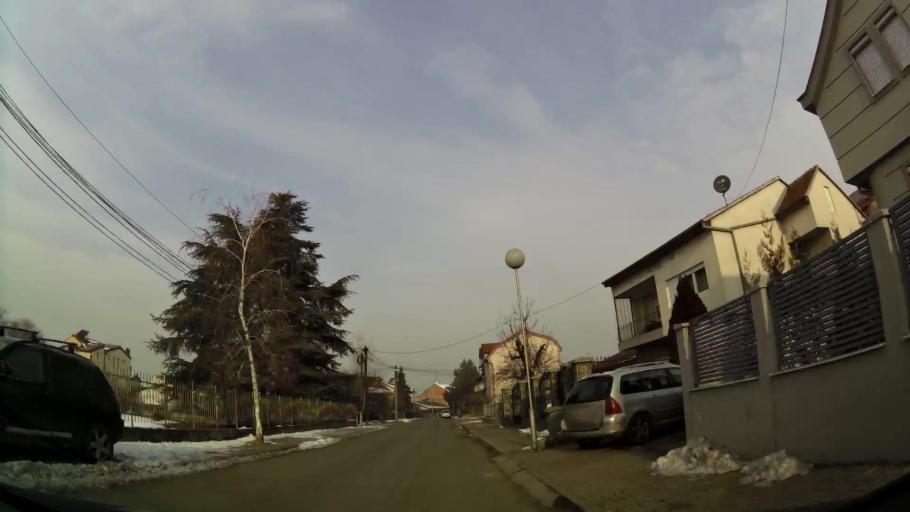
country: MK
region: Butel
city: Butel
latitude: 42.0218
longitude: 21.4529
